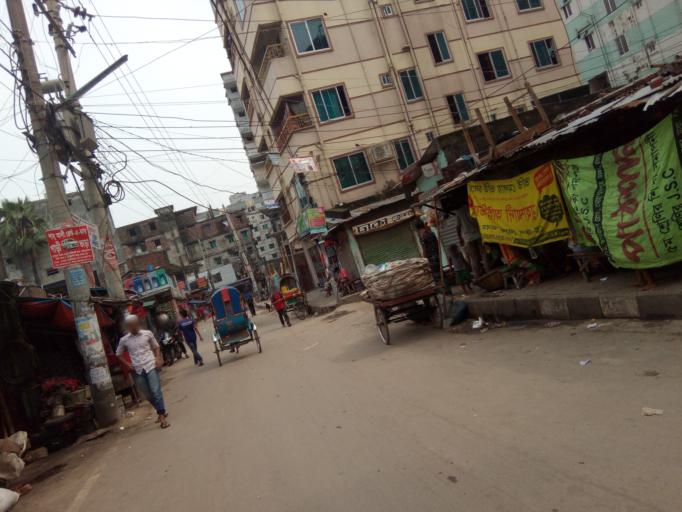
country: BD
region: Dhaka
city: Azimpur
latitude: 23.7563
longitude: 90.3602
